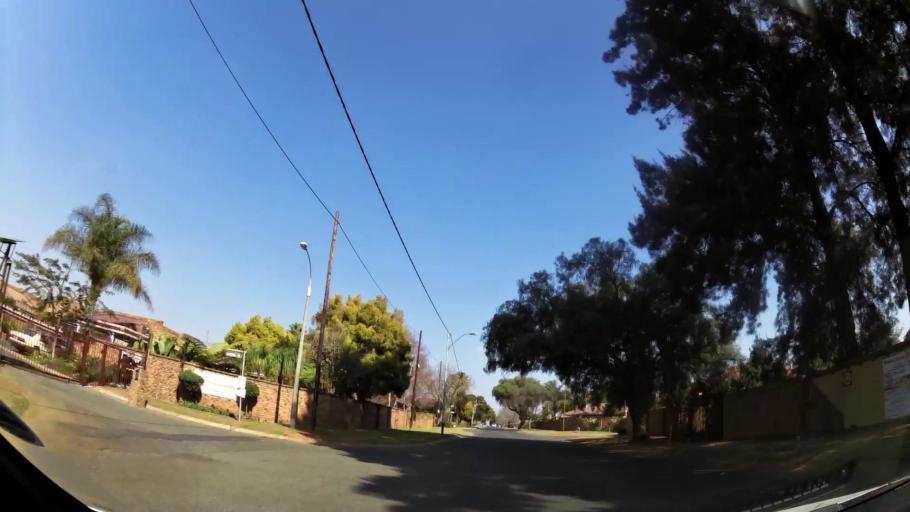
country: ZA
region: Gauteng
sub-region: Ekurhuleni Metropolitan Municipality
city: Boksburg
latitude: -26.1811
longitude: 28.2772
